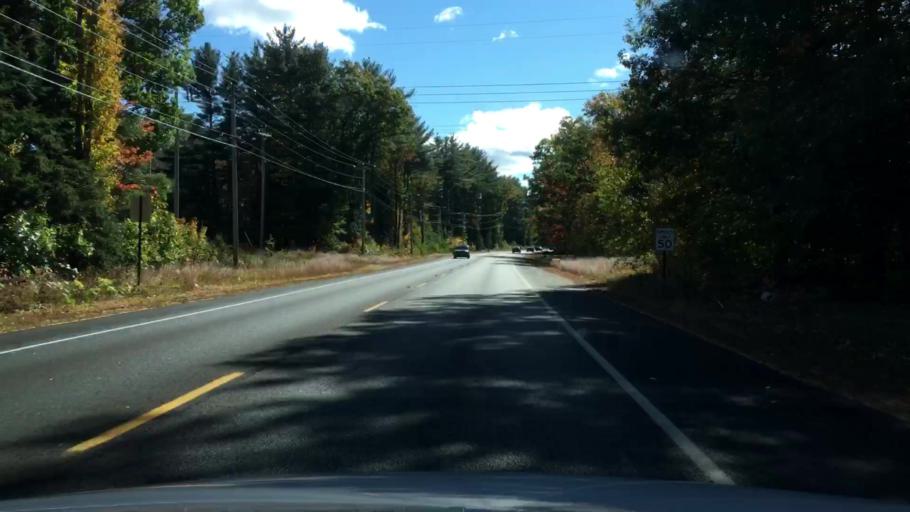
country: US
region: Maine
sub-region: York County
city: South Sanford
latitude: 43.4295
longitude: -70.7331
